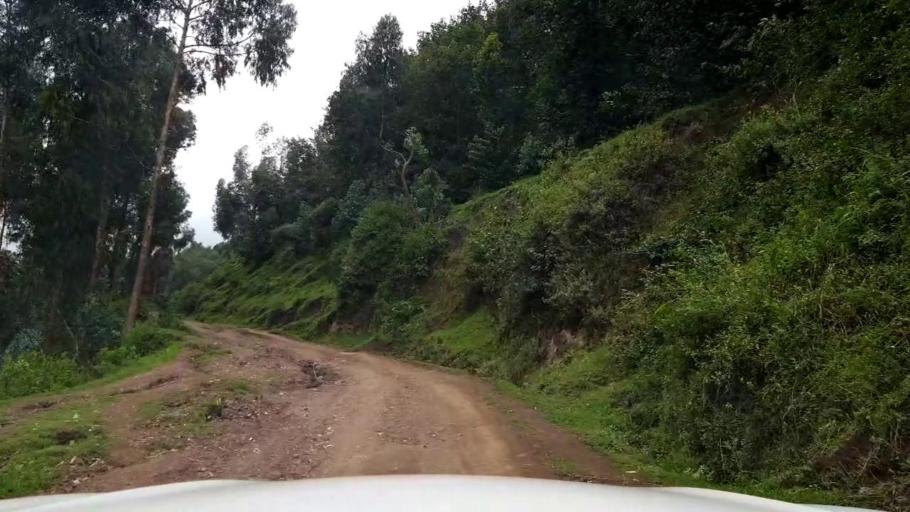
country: RW
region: Western Province
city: Gisenyi
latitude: -1.6507
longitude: 29.4154
